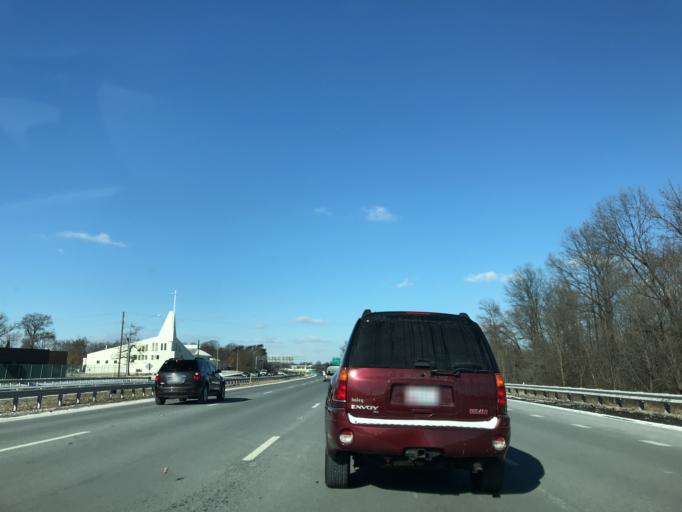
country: US
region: Maryland
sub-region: Prince George's County
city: Camp Springs
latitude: 38.8115
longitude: -76.9104
